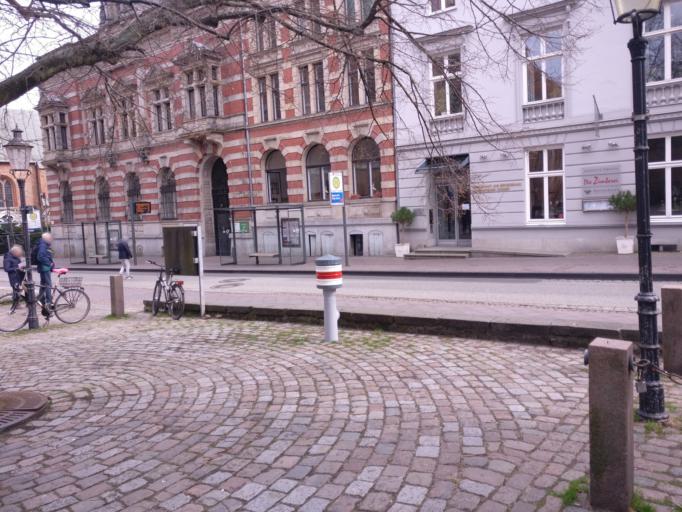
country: DE
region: Schleswig-Holstein
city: Luebeck
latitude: 53.8706
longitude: 10.6893
